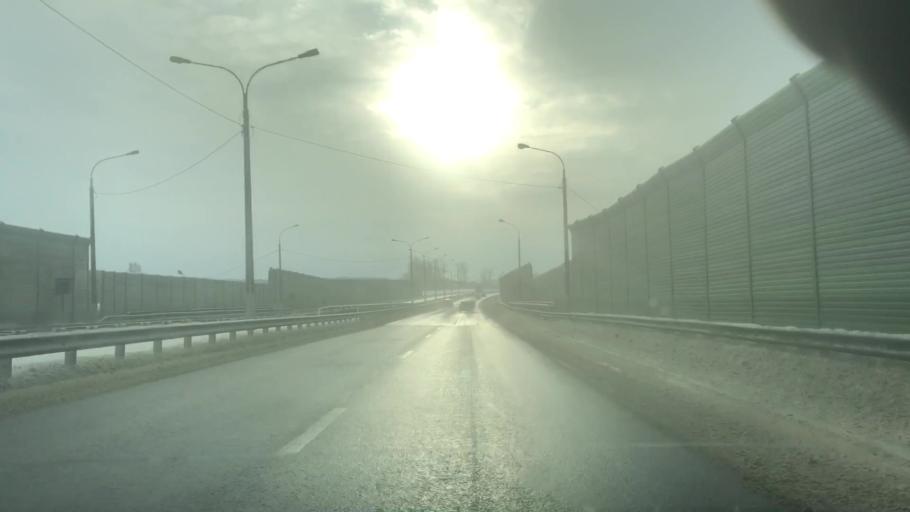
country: RU
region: Tula
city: Venev
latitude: 54.2777
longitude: 38.1600
